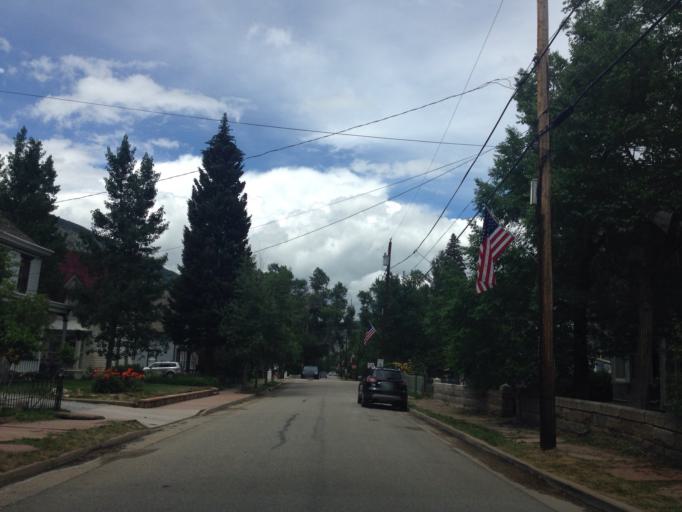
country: US
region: Colorado
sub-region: Clear Creek County
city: Georgetown
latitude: 39.7084
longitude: -105.6963
